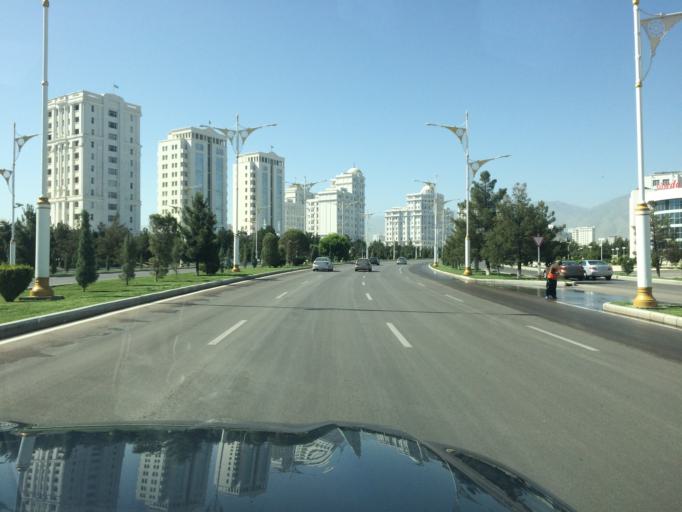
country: TM
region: Ahal
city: Ashgabat
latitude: 37.9054
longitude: 58.3654
